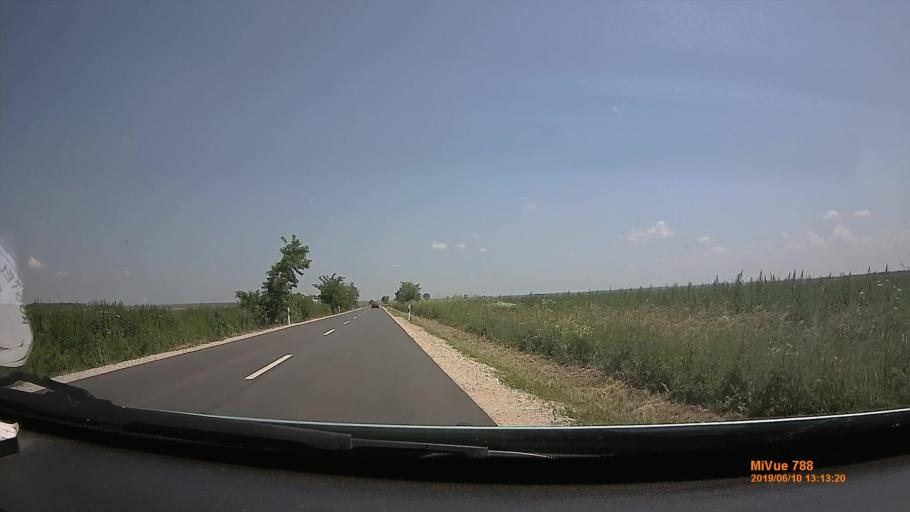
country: HU
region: Borsod-Abauj-Zemplen
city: Hernadnemeti
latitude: 48.0605
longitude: 21.0029
